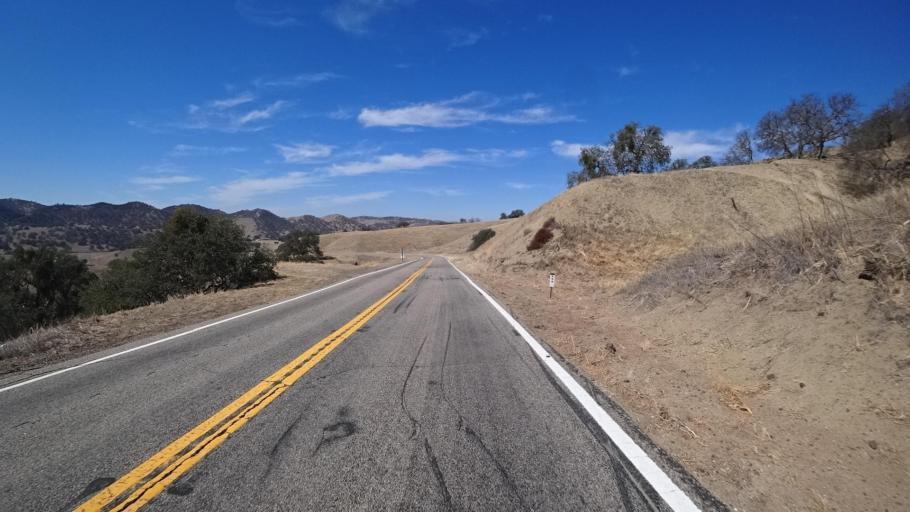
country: US
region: California
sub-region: Monterey County
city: King City
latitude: 36.1914
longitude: -120.8051
